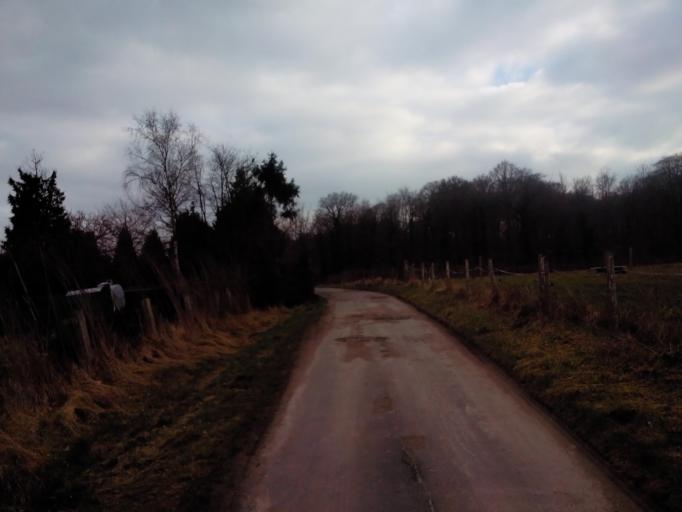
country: BE
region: Flanders
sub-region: Provincie Vlaams-Brabant
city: Oud-Heverlee
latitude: 50.8214
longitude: 4.7016
